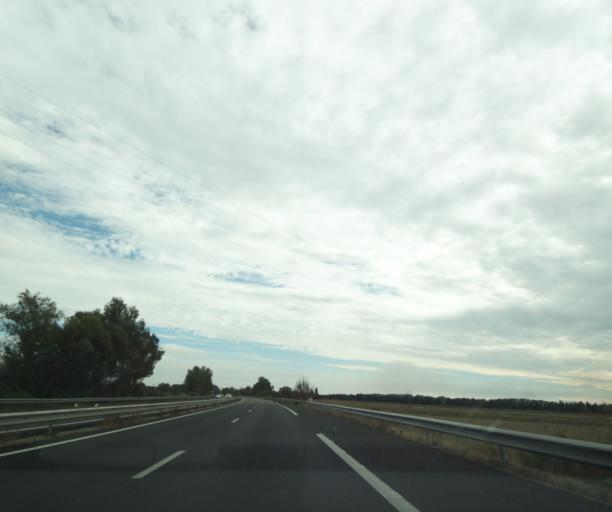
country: FR
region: Languedoc-Roussillon
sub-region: Departement du Gard
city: Bellegarde
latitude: 43.7147
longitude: 4.5124
